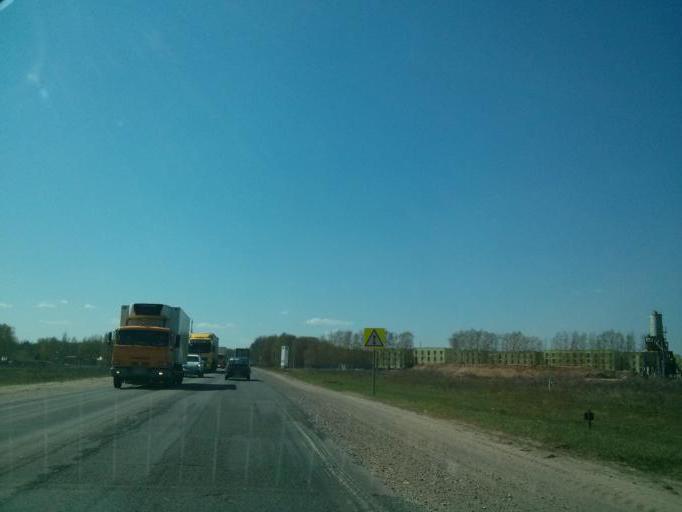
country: RU
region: Nizjnij Novgorod
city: Afonino
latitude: 56.2137
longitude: 44.0280
